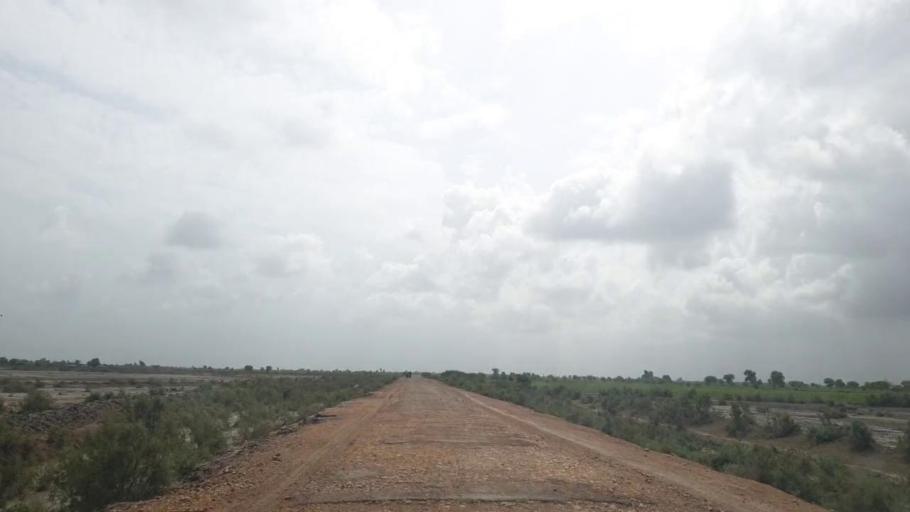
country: PK
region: Sindh
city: Tando Bago
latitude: 24.8280
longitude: 69.0893
